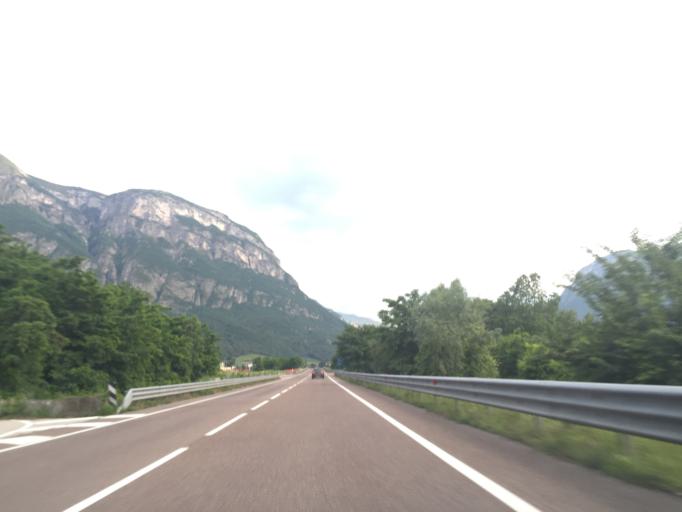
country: IT
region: Trentino-Alto Adige
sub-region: Provincia di Trento
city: Mattarello
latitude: 46.0042
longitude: 11.1234
